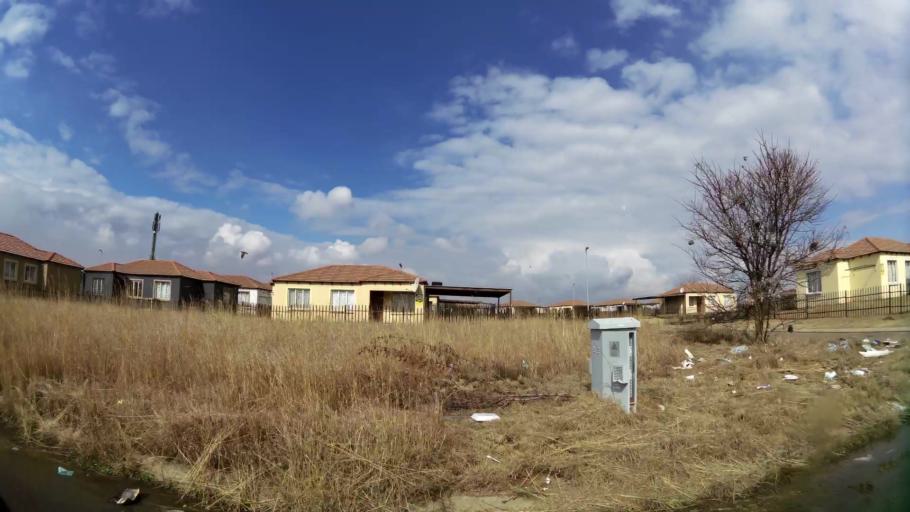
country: ZA
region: Gauteng
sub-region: Sedibeng District Municipality
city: Vanderbijlpark
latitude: -26.7151
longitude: 27.8823
